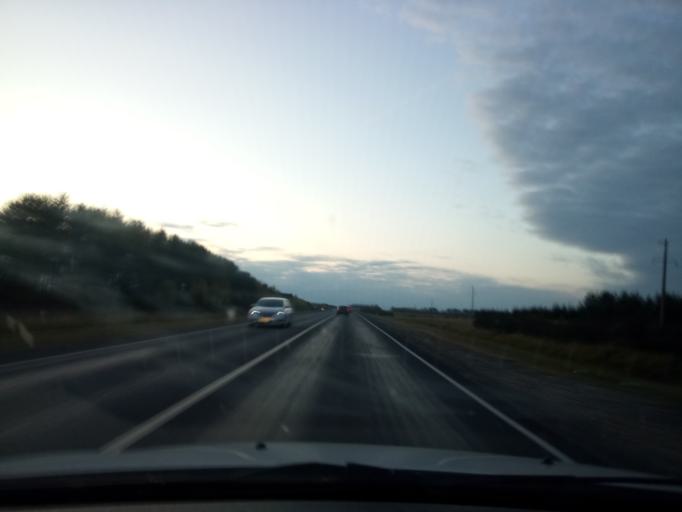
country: RU
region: Nizjnij Novgorod
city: Bol'shoye Murashkino
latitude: 55.8948
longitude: 44.7333
